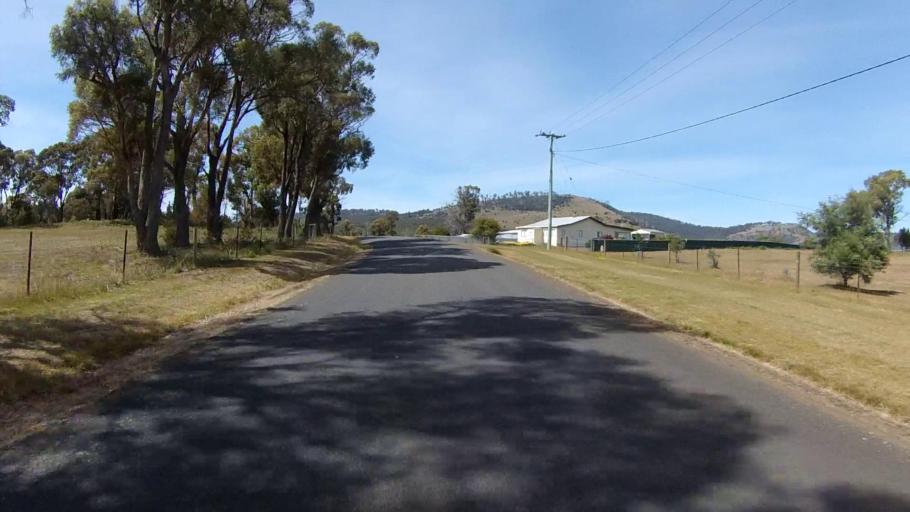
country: AU
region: Tasmania
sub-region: Sorell
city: Sorell
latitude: -42.6149
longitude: 147.7280
